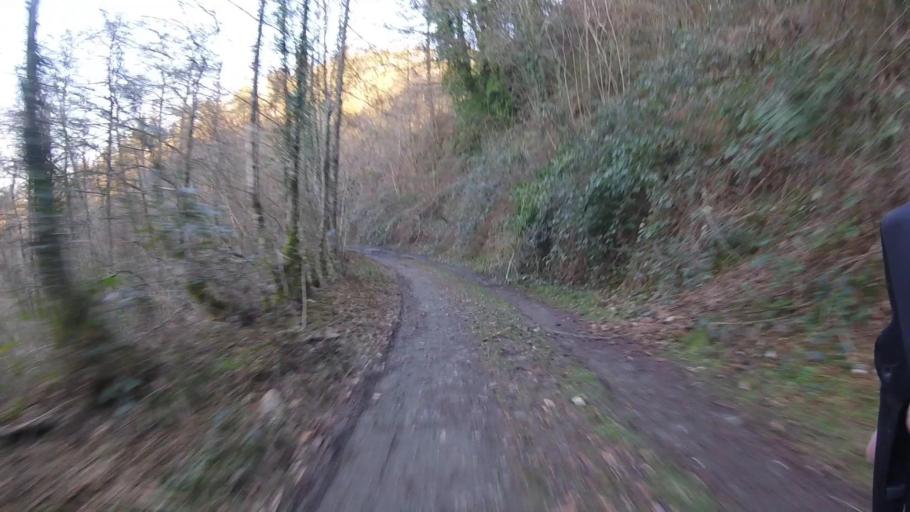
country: ES
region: Navarre
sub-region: Provincia de Navarra
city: Arano
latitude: 43.2392
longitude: -1.8651
